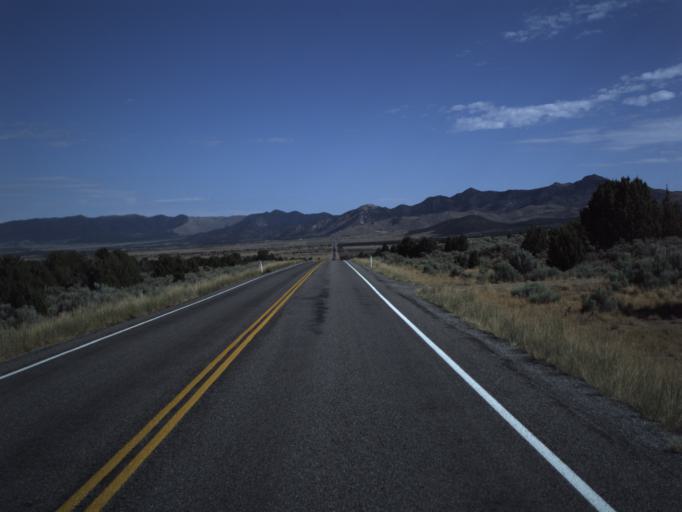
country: US
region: Utah
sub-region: Juab County
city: Mona
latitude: 39.8403
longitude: -112.1381
